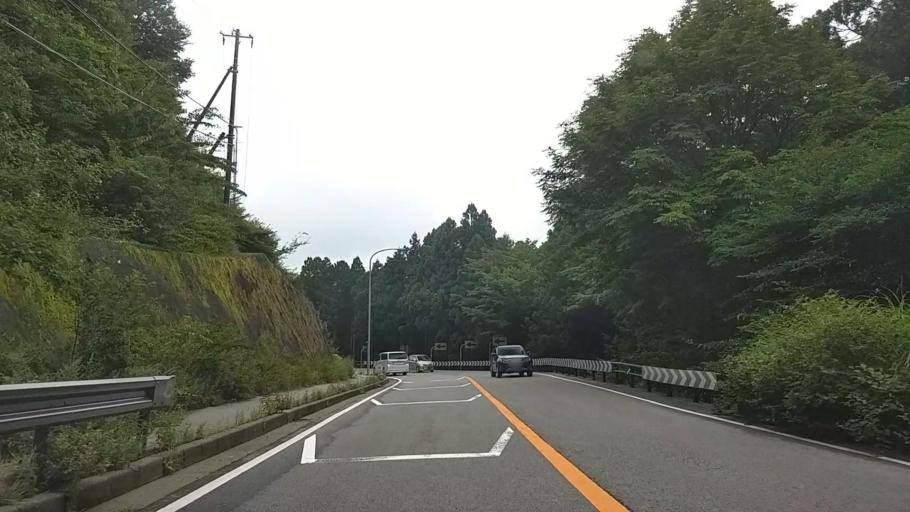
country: JP
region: Yamanashi
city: Fujikawaguchiko
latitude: 35.4578
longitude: 138.6089
